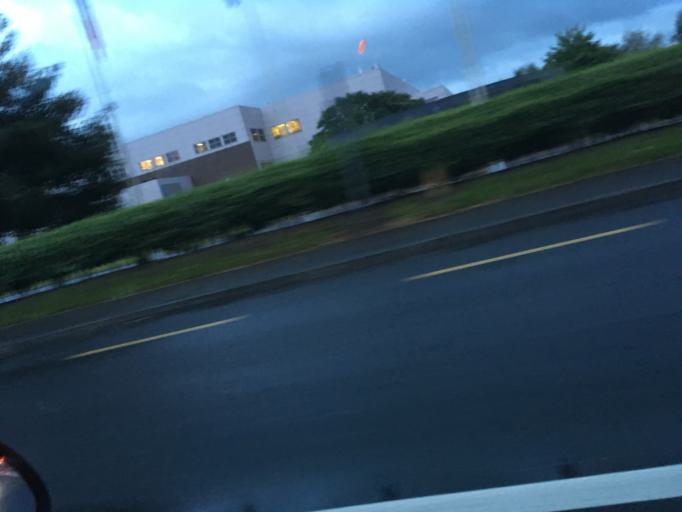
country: IE
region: Leinster
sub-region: Kildare
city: Droichead Nua
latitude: 53.1871
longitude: -6.7830
